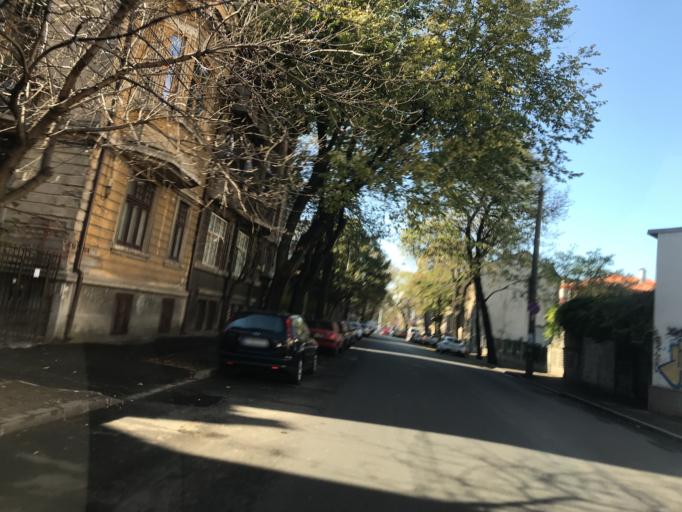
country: RO
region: Bucuresti
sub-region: Municipiul Bucuresti
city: Bucuresti
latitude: 44.4433
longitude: 26.0838
